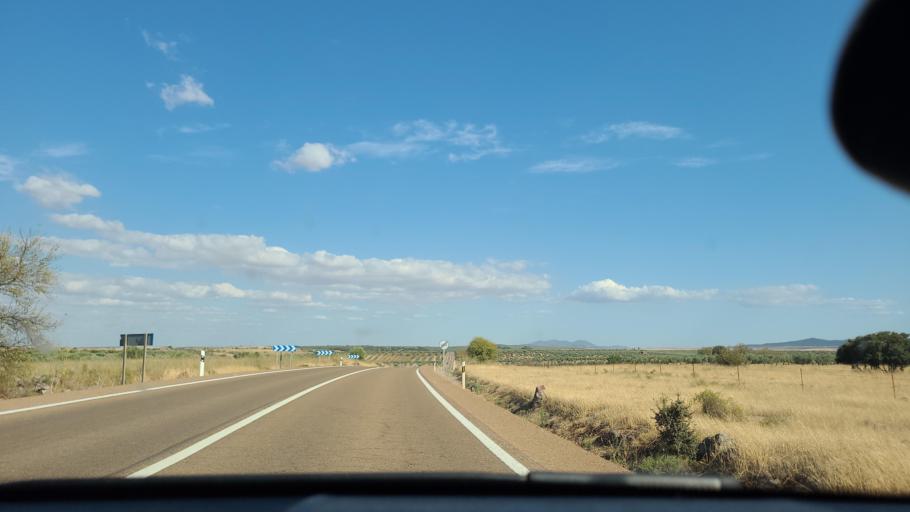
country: ES
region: Extremadura
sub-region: Provincia de Badajoz
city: Usagre
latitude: 38.3514
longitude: -6.1942
